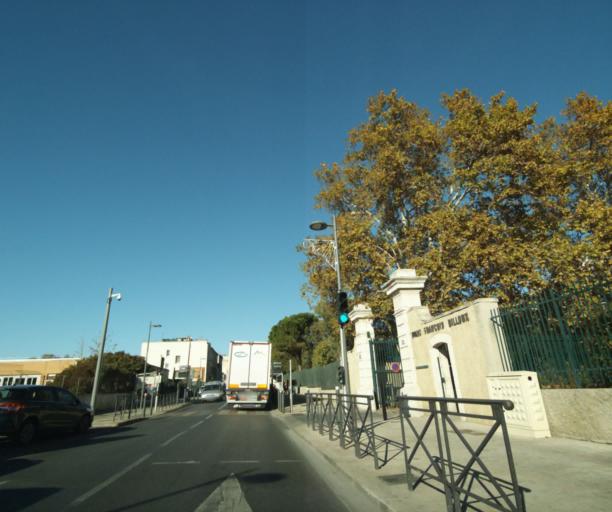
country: FR
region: Provence-Alpes-Cote d'Azur
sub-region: Departement des Bouches-du-Rhone
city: Marseille 14
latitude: 43.3322
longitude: 5.3646
